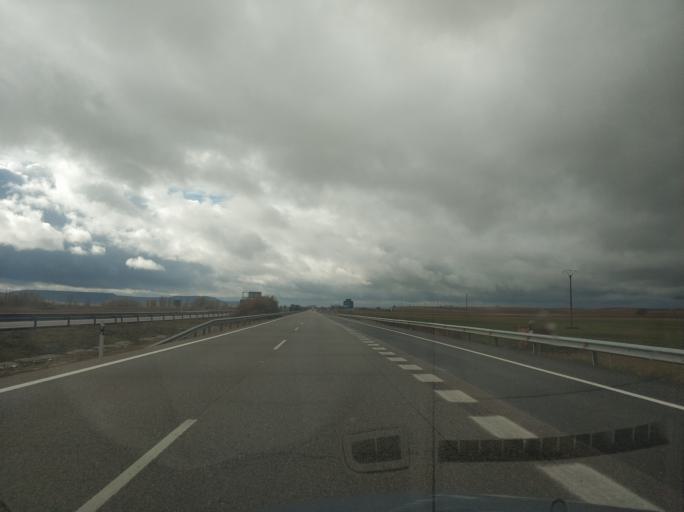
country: ES
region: Castille and Leon
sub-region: Provincia de Palencia
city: Torquemada
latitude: 42.0254
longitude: -4.3310
